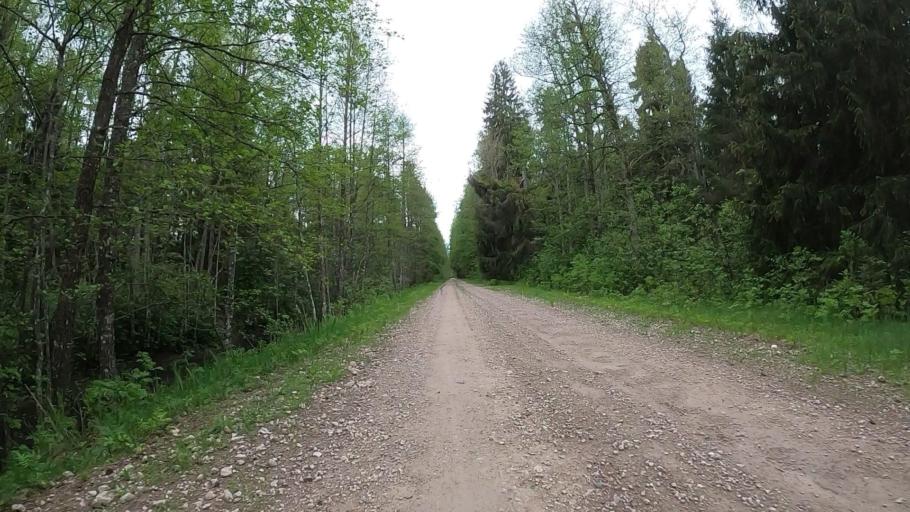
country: LV
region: Ozolnieku
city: Ozolnieki
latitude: 56.8055
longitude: 23.7857
